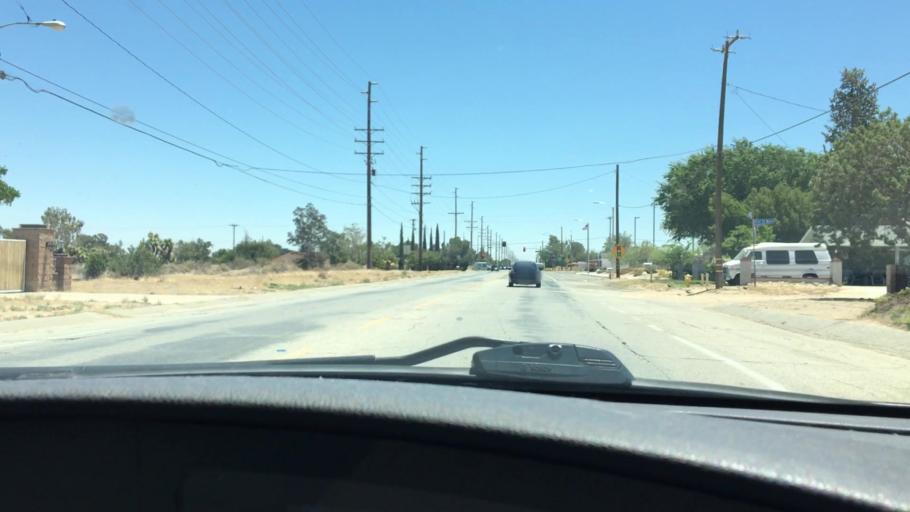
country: US
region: California
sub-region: Los Angeles County
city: Quartz Hill
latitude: 34.6602
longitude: -118.2214
